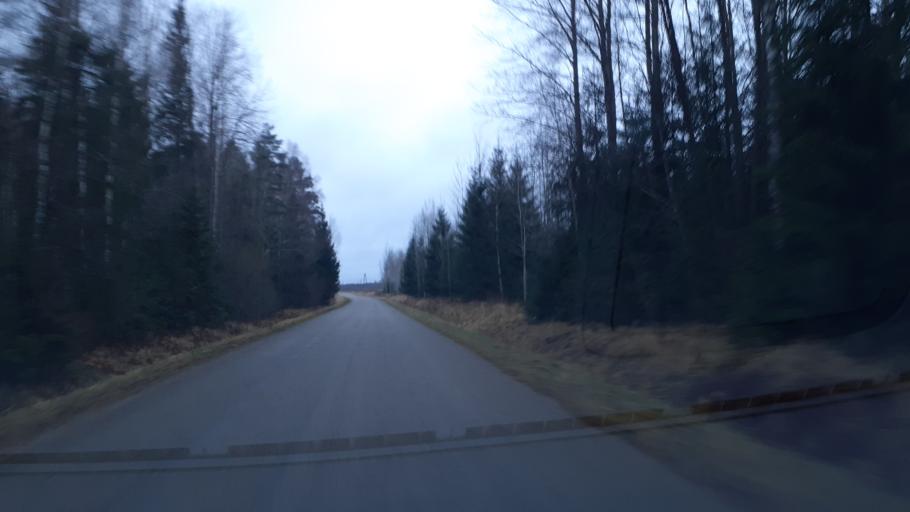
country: LV
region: Kuldigas Rajons
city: Kuldiga
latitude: 57.0353
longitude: 22.1549
